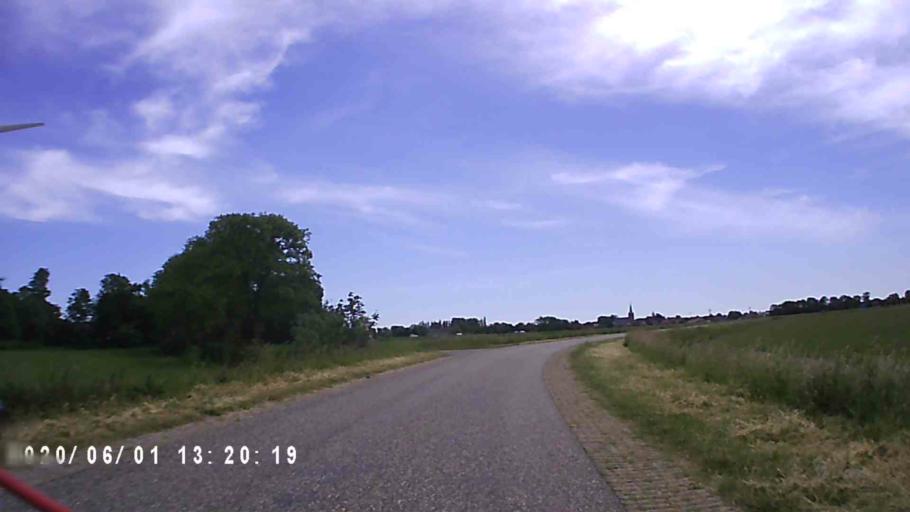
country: NL
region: Friesland
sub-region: Gemeente Littenseradiel
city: Wommels
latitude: 53.1145
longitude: 5.5820
